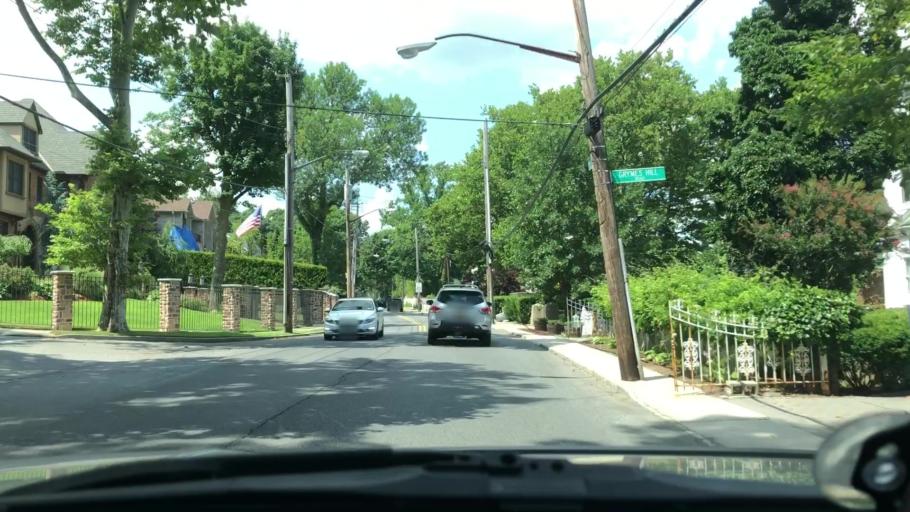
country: US
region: New Jersey
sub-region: Hudson County
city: Bayonne
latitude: 40.6233
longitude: -74.0885
